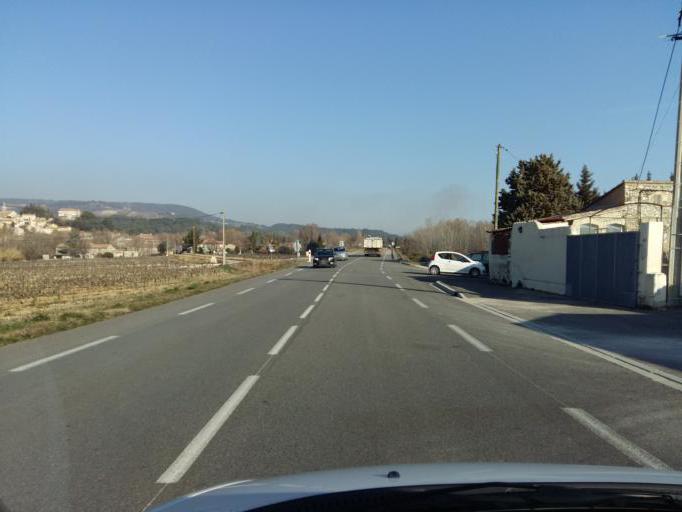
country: FR
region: Provence-Alpes-Cote d'Azur
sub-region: Departement du Vaucluse
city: Sablet
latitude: 44.2398
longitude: 5.0165
